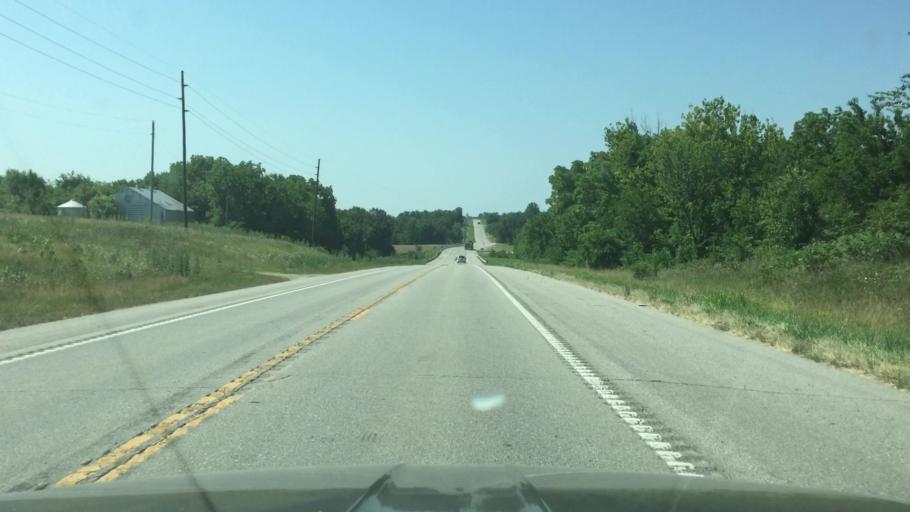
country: US
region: Missouri
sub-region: Moniteau County
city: Tipton
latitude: 38.6336
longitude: -92.7892
